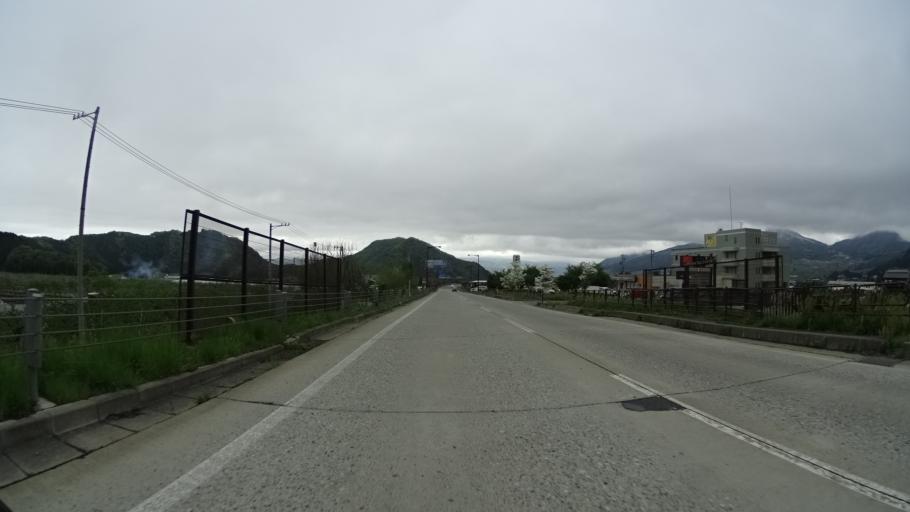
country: JP
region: Nagano
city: Nakano
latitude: 36.7400
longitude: 138.4069
